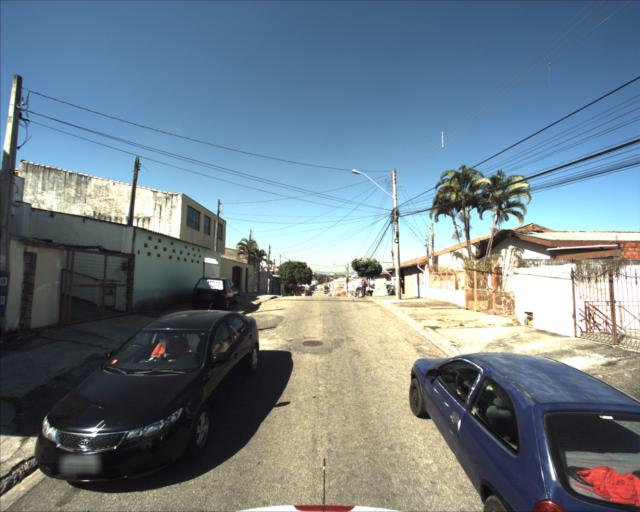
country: BR
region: Sao Paulo
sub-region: Sorocaba
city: Sorocaba
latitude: -23.5070
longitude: -47.4289
